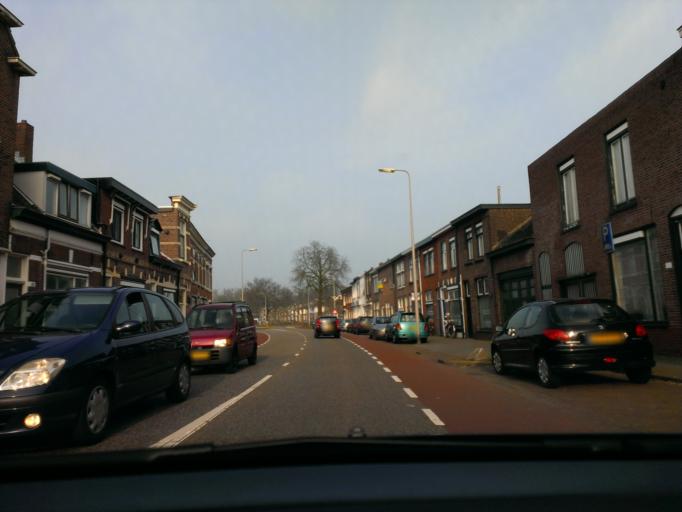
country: NL
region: Overijssel
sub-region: Gemeente Zwolle
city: Zwolle
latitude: 52.5167
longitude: 6.1070
